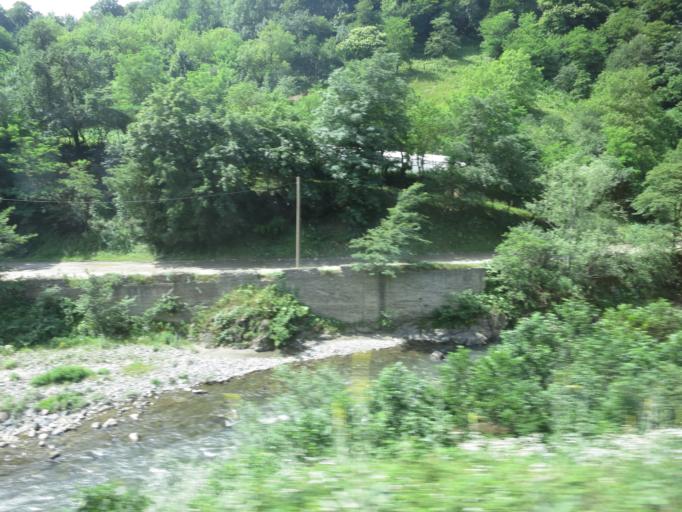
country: GE
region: Imereti
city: Kharagauli
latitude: 42.0050
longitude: 43.2205
